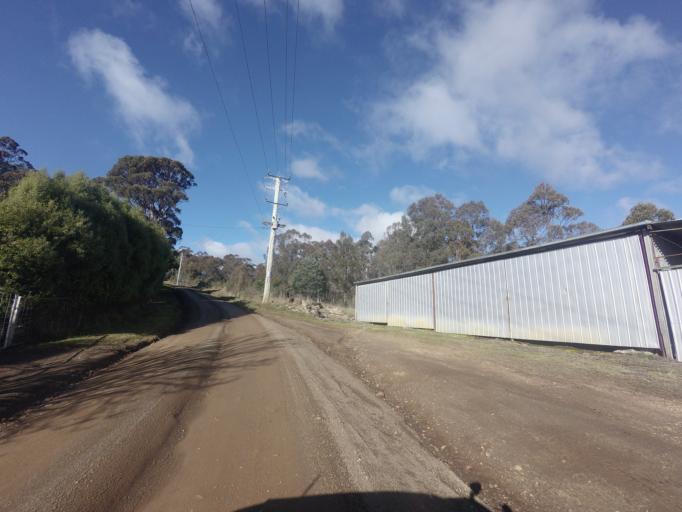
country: AU
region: Tasmania
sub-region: Derwent Valley
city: New Norfolk
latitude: -42.8409
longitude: 147.1366
